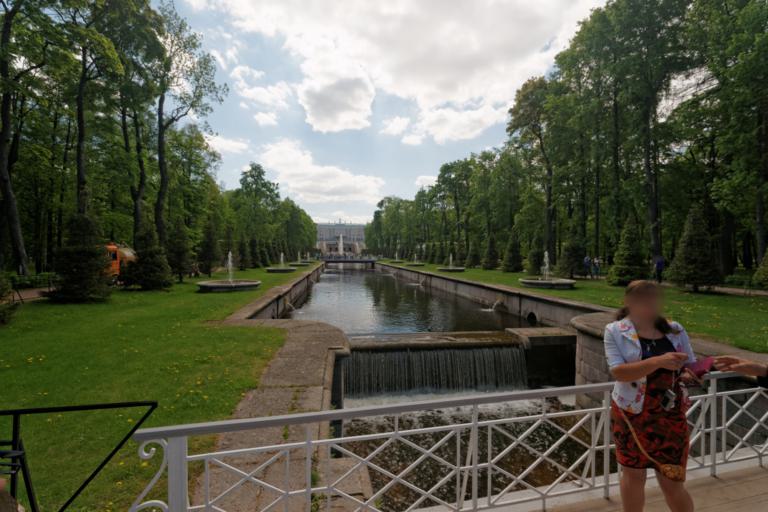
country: RU
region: St.-Petersburg
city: Peterhof
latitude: 59.8876
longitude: 29.9104
